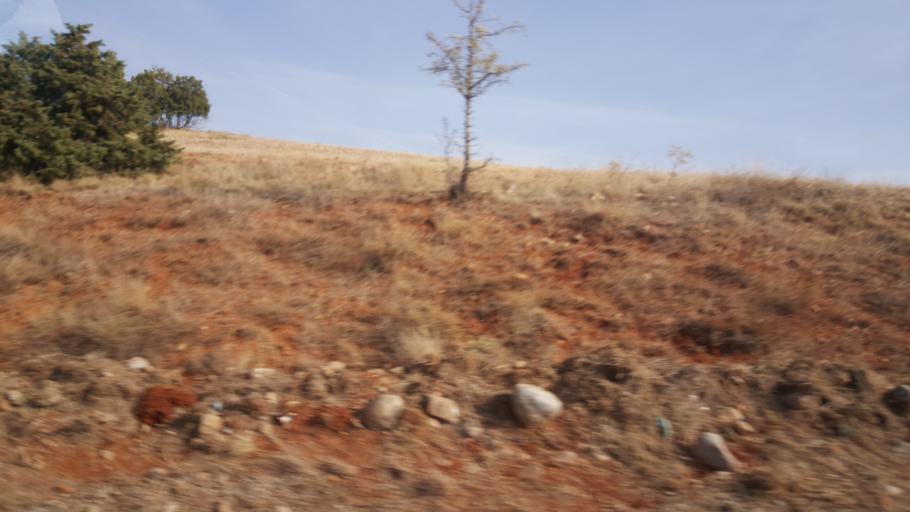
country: TR
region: Eskisehir
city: Mihaliccik
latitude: 39.9631
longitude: 31.3876
